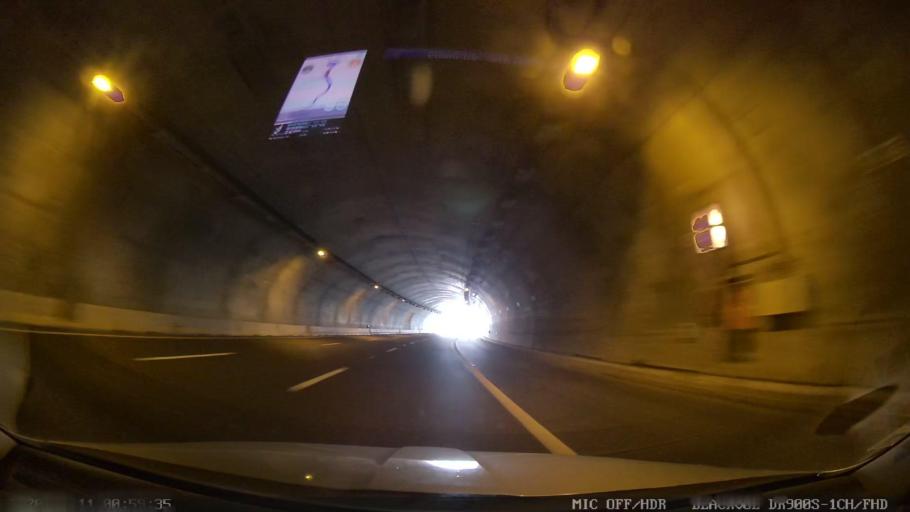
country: PT
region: Lisbon
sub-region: Arruda Dos Vinhos
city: Arruda dos Vinhos
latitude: 38.9424
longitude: -9.0679
